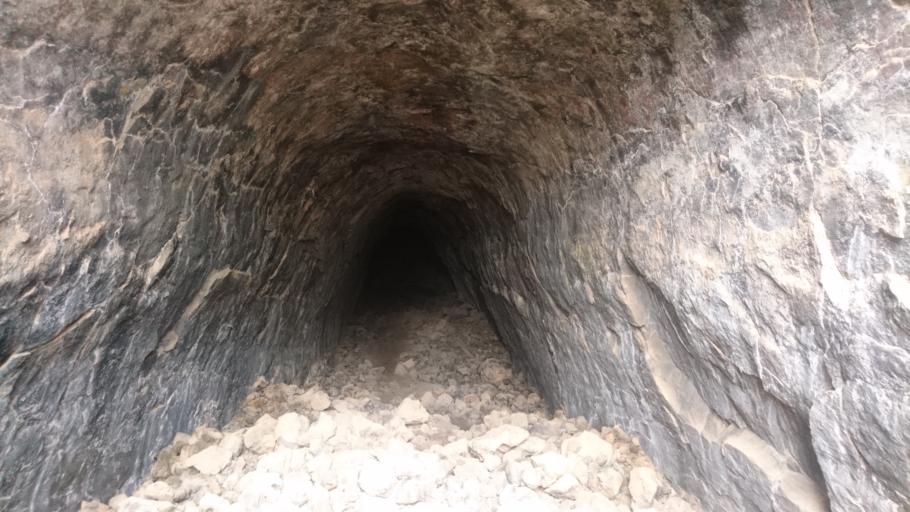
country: ES
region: Canary Islands
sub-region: Provincia de Santa Cruz de Tenerife
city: Guia de Isora
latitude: 28.2505
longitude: -16.7767
